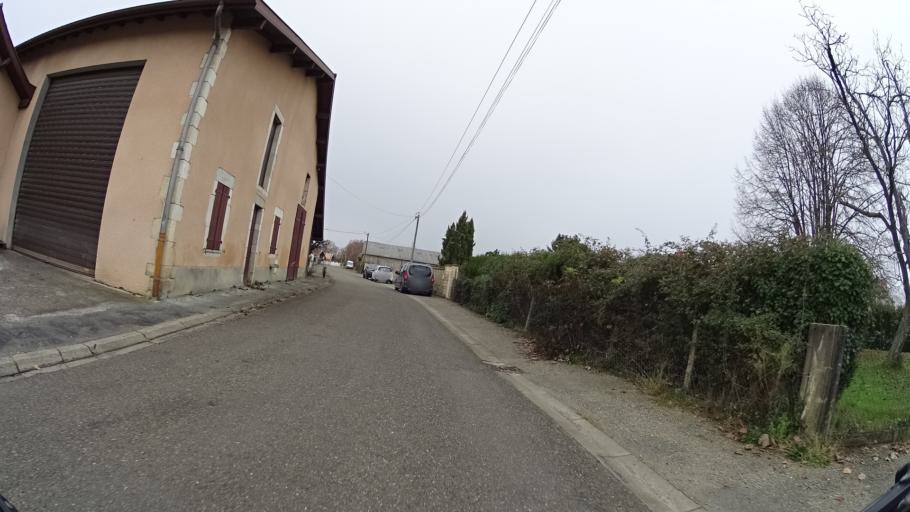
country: FR
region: Aquitaine
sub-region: Departement des Landes
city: Saint-Paul-les-Dax
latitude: 43.7318
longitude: -1.0504
